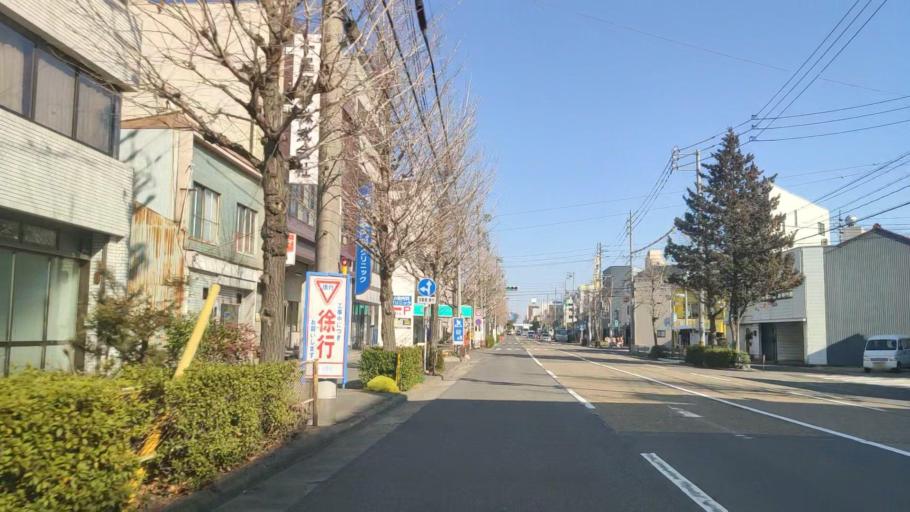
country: JP
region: Gifu
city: Gifu-shi
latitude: 35.4151
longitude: 136.7501
